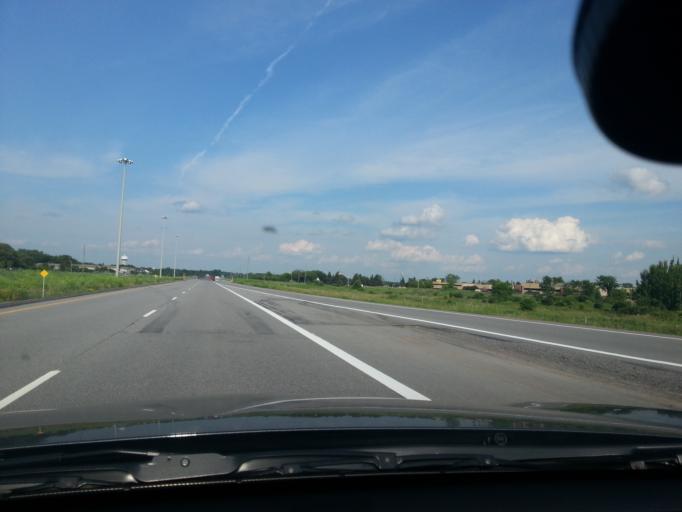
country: CA
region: Ontario
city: Arnprior
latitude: 45.4201
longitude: -76.3679
